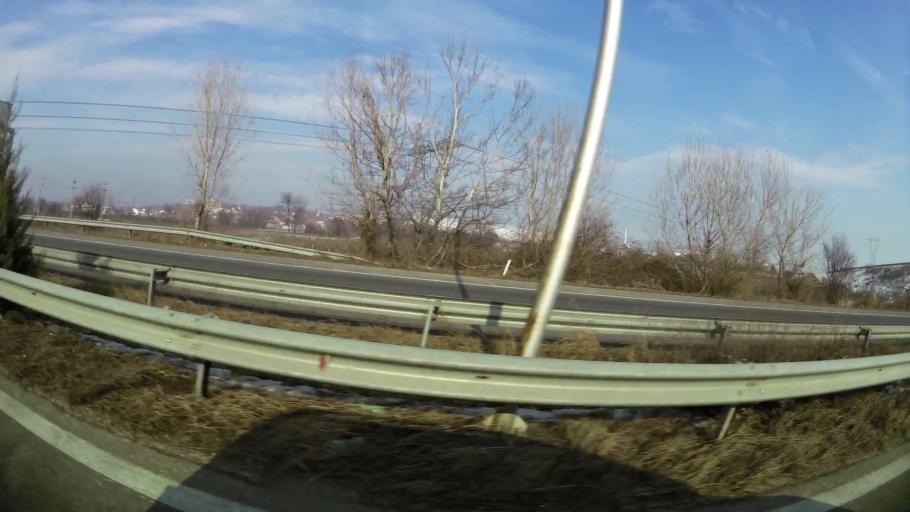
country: MK
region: Butel
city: Butel
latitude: 42.0397
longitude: 21.4612
